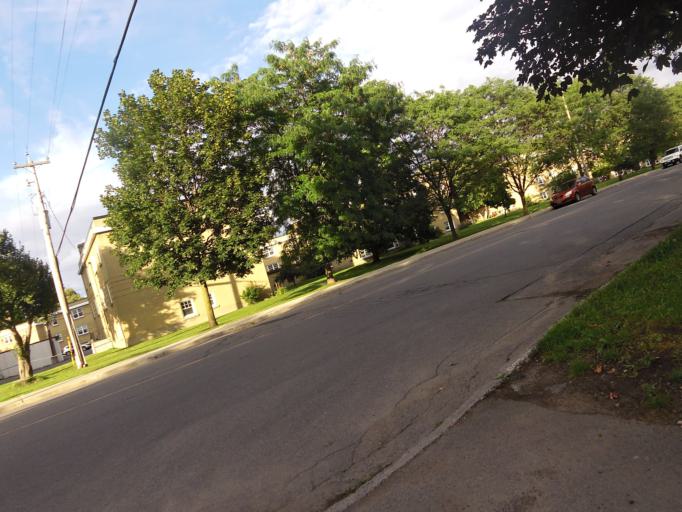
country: CA
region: Ontario
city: Ottawa
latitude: 45.3807
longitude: -75.7704
